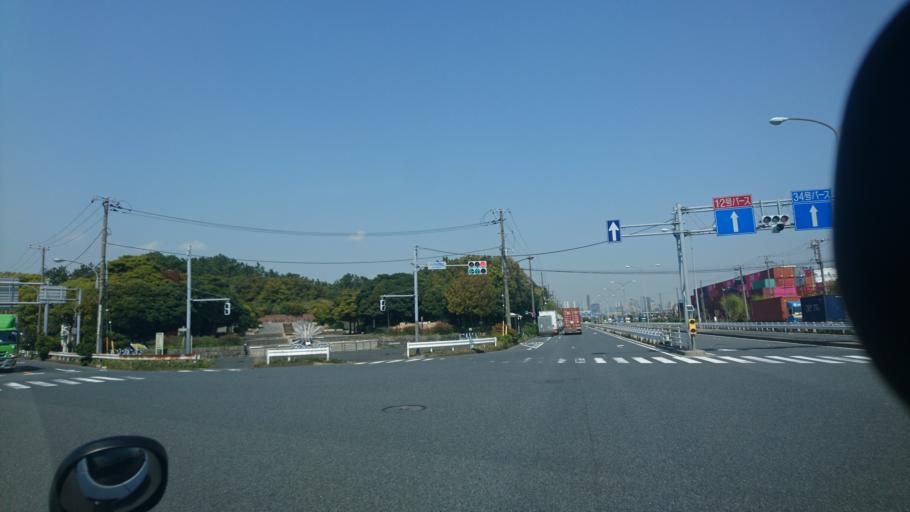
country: JP
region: Kanagawa
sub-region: Kawasaki-shi
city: Kawasaki
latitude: 35.5950
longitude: 139.7651
